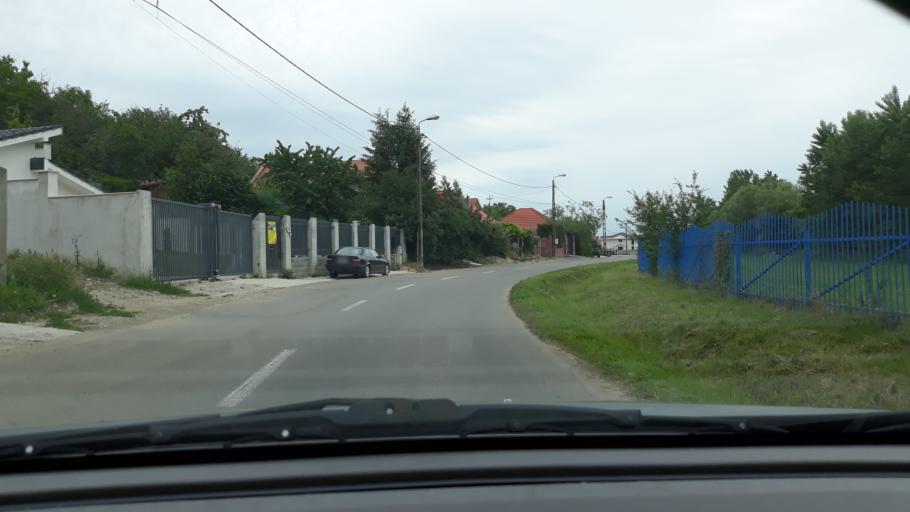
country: RO
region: Bihor
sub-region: Comuna Sanmartin
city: Sanmartin
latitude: 47.0513
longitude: 21.9917
